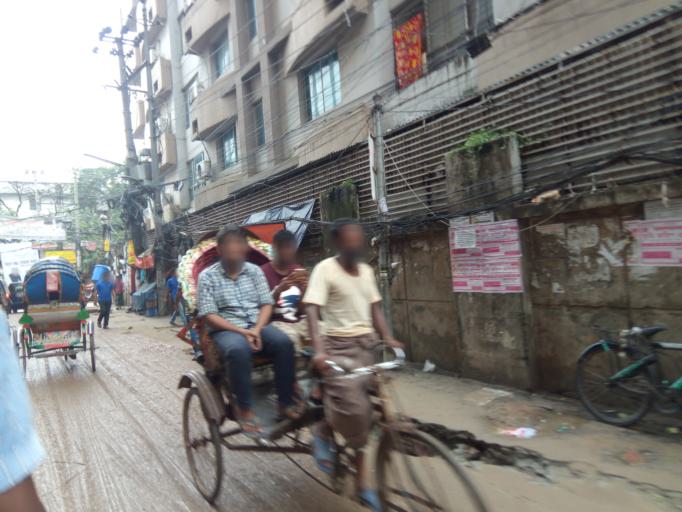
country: BD
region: Dhaka
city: Azimpur
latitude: 23.7481
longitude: 90.3868
